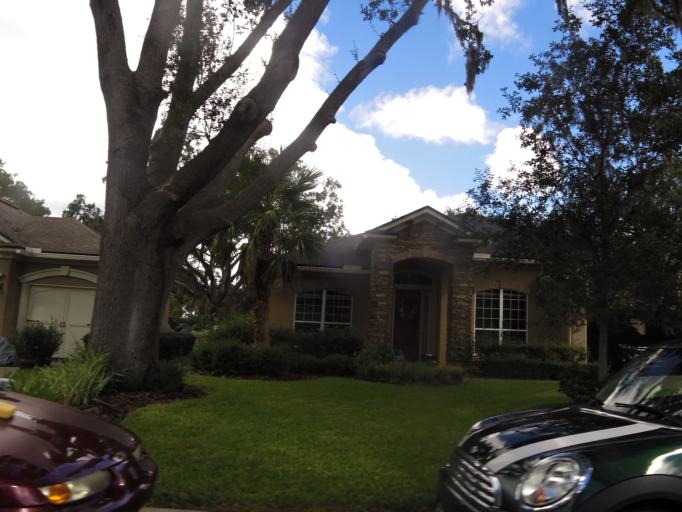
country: US
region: Florida
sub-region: Nassau County
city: Fernandina Beach
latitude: 30.6273
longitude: -81.4612
